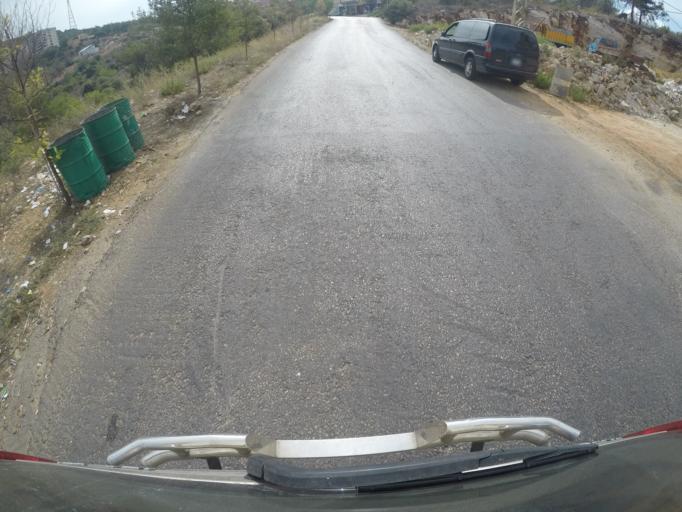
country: LB
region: Mont-Liban
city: Beit ed Dine
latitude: 33.7356
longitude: 35.4847
